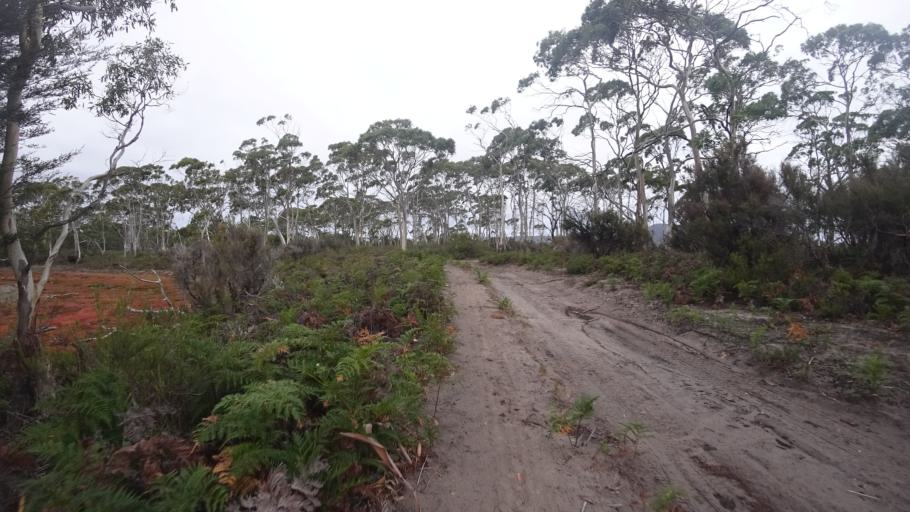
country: AU
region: Tasmania
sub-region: Sorell
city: Sorell
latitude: -42.6537
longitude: 148.0457
